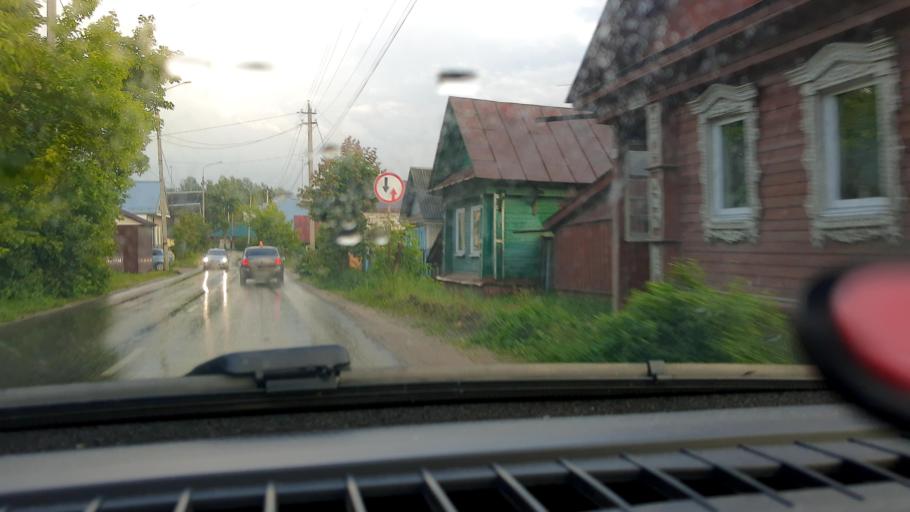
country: RU
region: Nizjnij Novgorod
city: Gorodets
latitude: 56.6579
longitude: 43.4630
